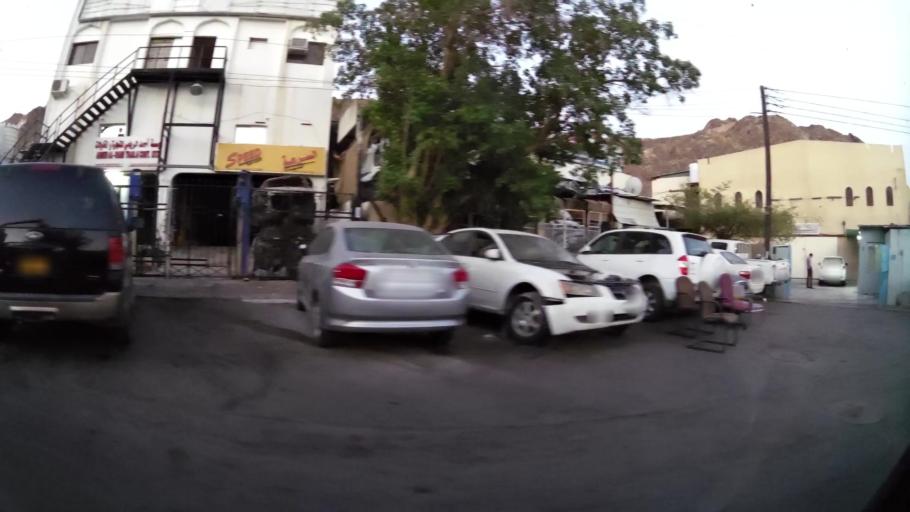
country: OM
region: Muhafazat Masqat
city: Muscat
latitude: 23.5962
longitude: 58.5621
